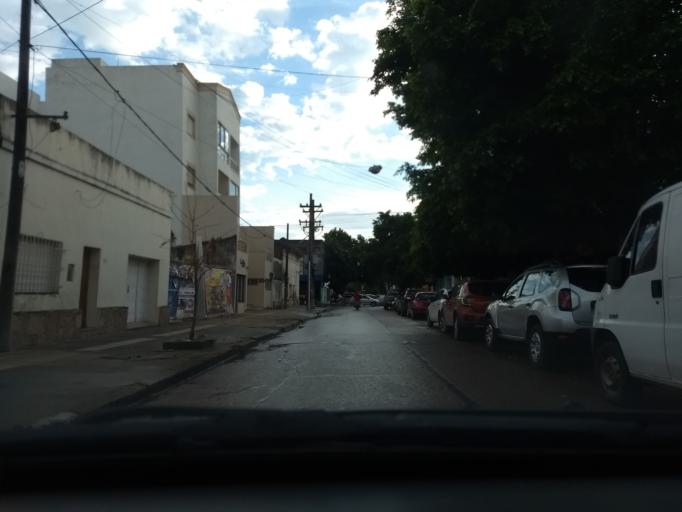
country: AR
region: Corrientes
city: Corrientes
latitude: -27.4723
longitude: -58.8283
